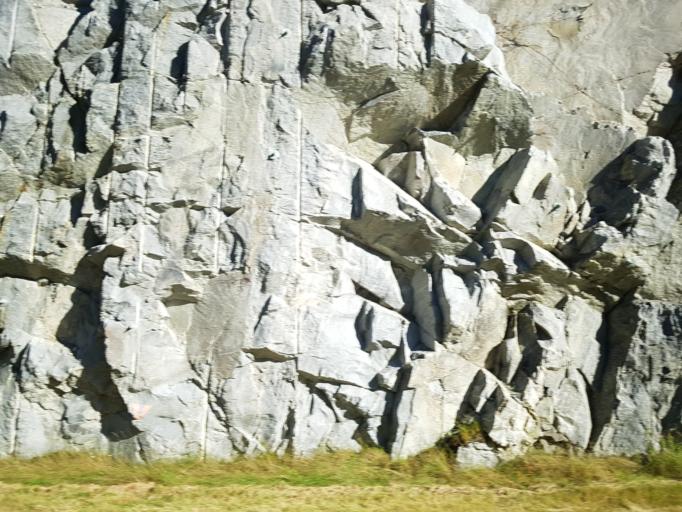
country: NO
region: Sor-Trondelag
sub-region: Afjord
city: A i Afjord
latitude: 63.7703
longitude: 10.2366
